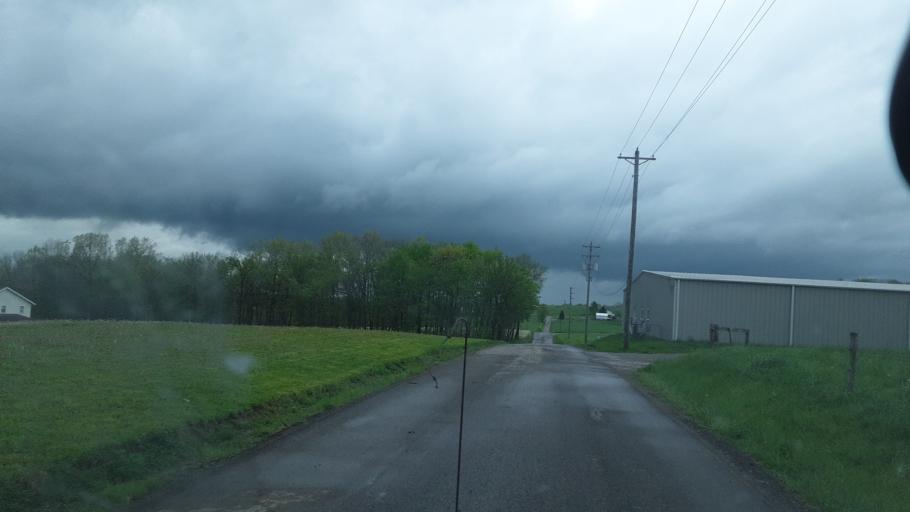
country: US
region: Ohio
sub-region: Holmes County
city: Millersburg
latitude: 40.5897
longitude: -81.9453
